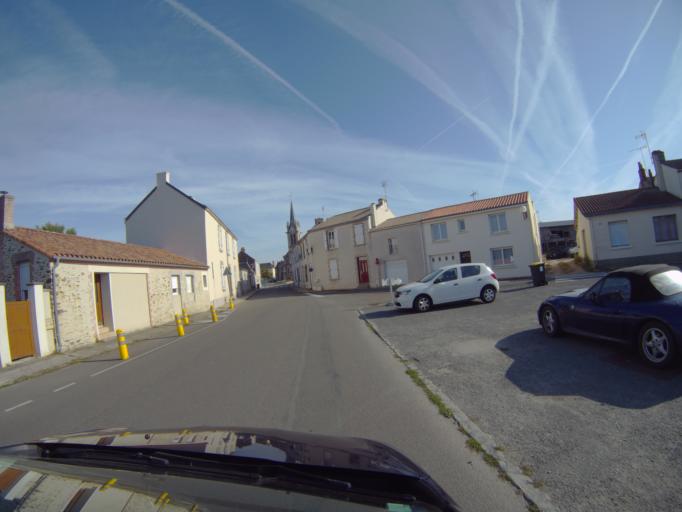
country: FR
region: Pays de la Loire
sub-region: Departement de la Vendee
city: Nieul-le-Dolent
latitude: 46.5741
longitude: -1.5097
